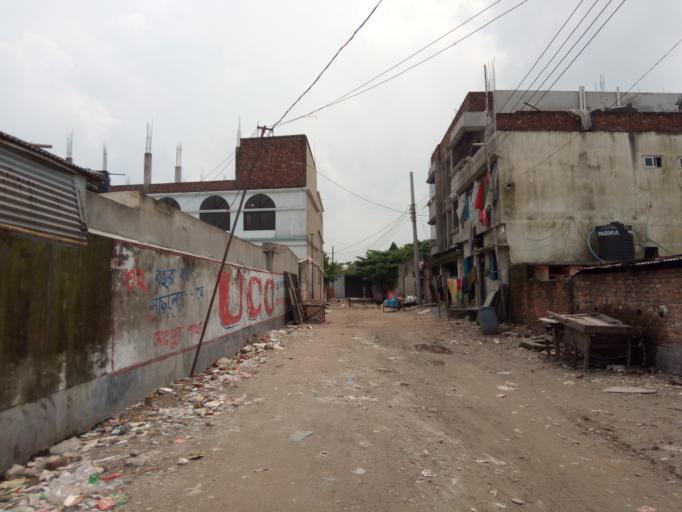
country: BD
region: Dhaka
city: Azimpur
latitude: 23.7546
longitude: 90.3528
